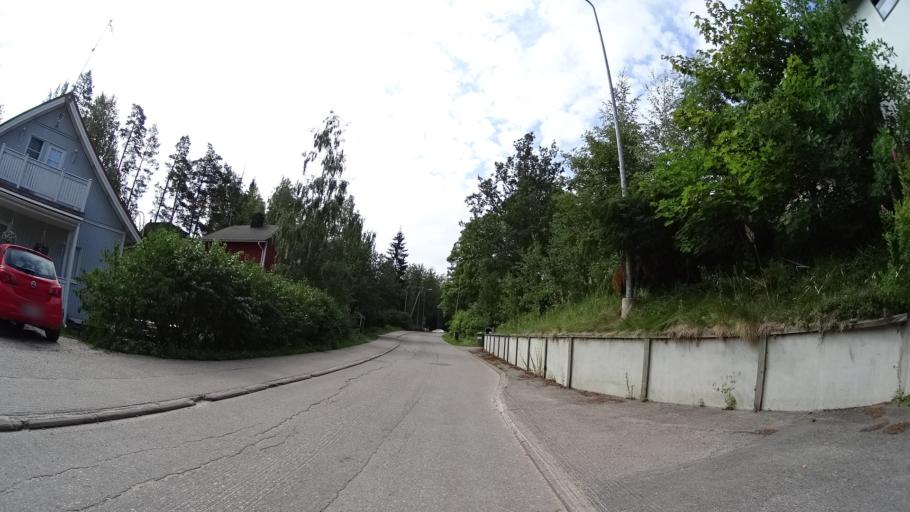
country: FI
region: Uusimaa
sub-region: Helsinki
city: Espoo
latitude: 60.2010
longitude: 24.6060
